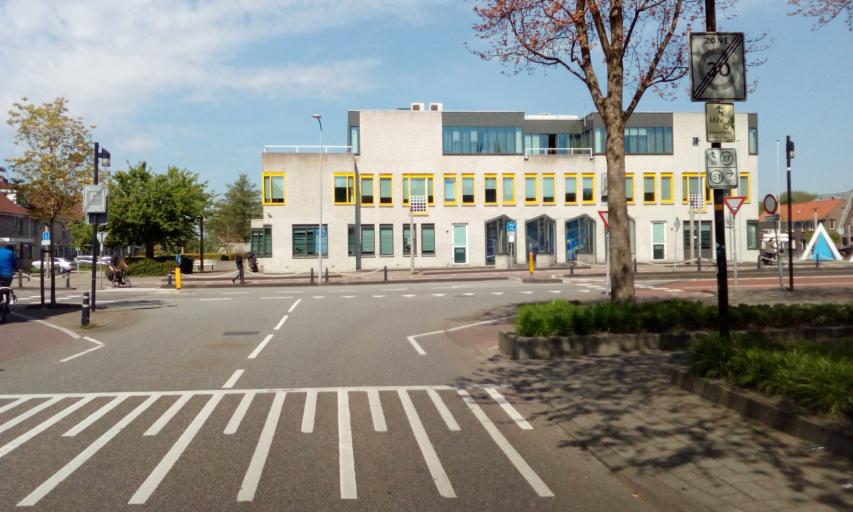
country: NL
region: North Holland
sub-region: Gemeente Uithoorn
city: Uithoorn
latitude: 52.2324
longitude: 4.8274
